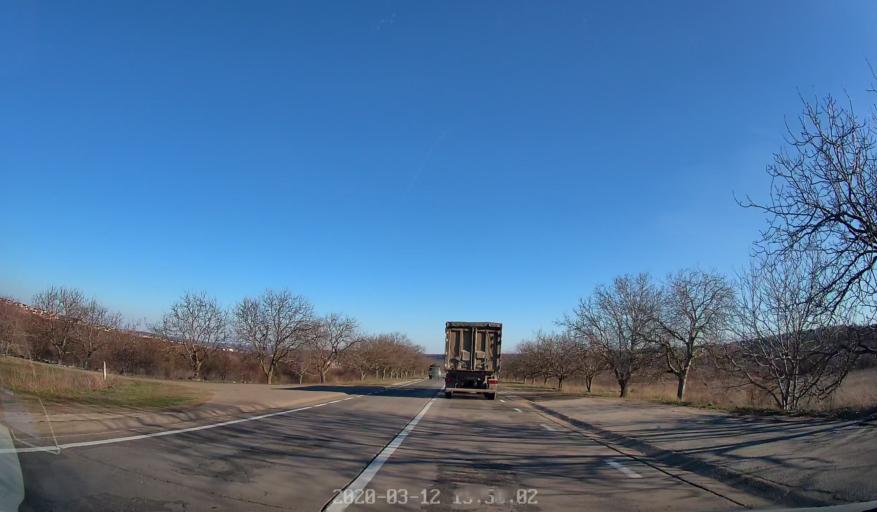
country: MD
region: Chisinau
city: Ciorescu
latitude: 47.0765
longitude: 28.9501
